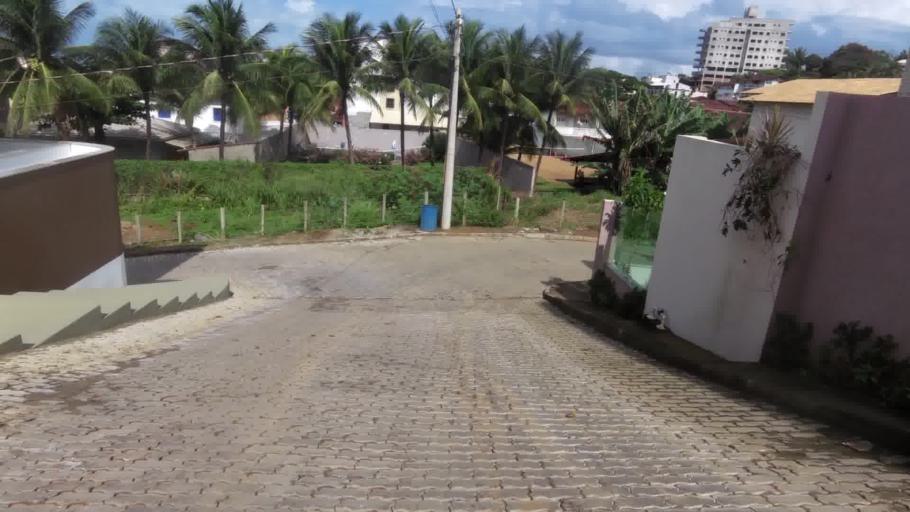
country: BR
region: Espirito Santo
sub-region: Piuma
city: Piuma
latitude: -20.8279
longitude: -40.6915
